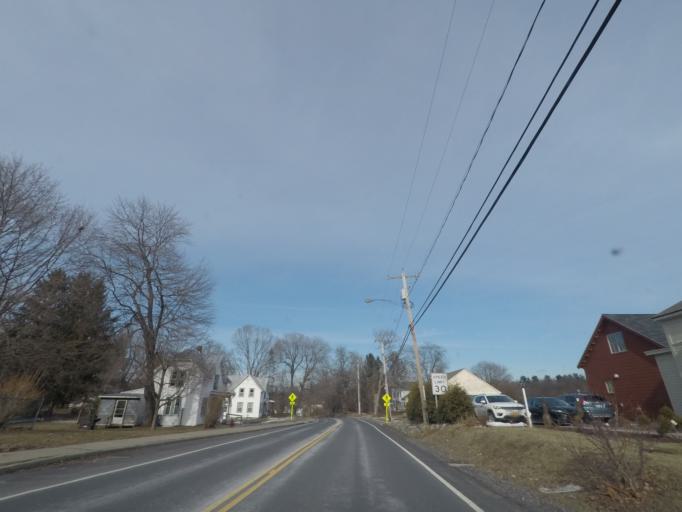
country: US
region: New York
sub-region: Columbia County
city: Valatie
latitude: 42.4105
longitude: -73.6739
